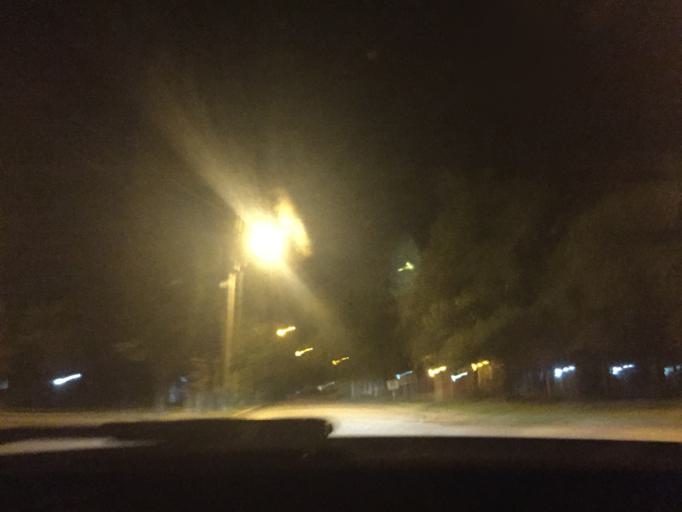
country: AR
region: Cordoba
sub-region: Departamento de Calamuchita
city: Santa Rosa de Calamuchita
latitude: -32.0743
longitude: -64.5325
